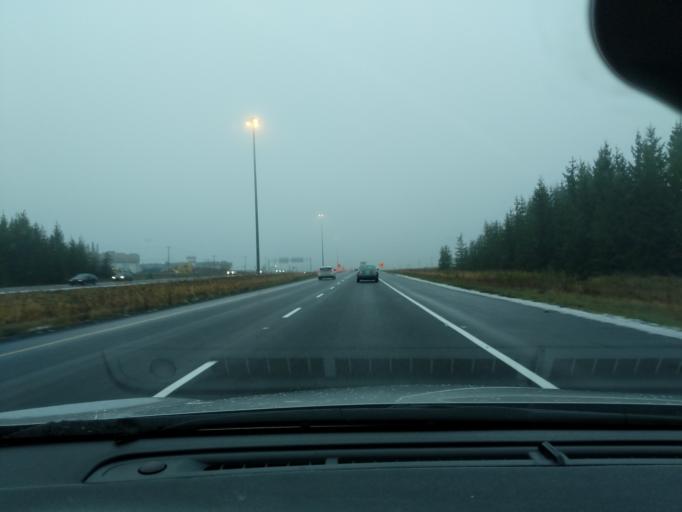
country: CA
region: Quebec
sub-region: Capitale-Nationale
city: Saint-Augustin-de-Desmaures
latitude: 46.7550
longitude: -71.4258
